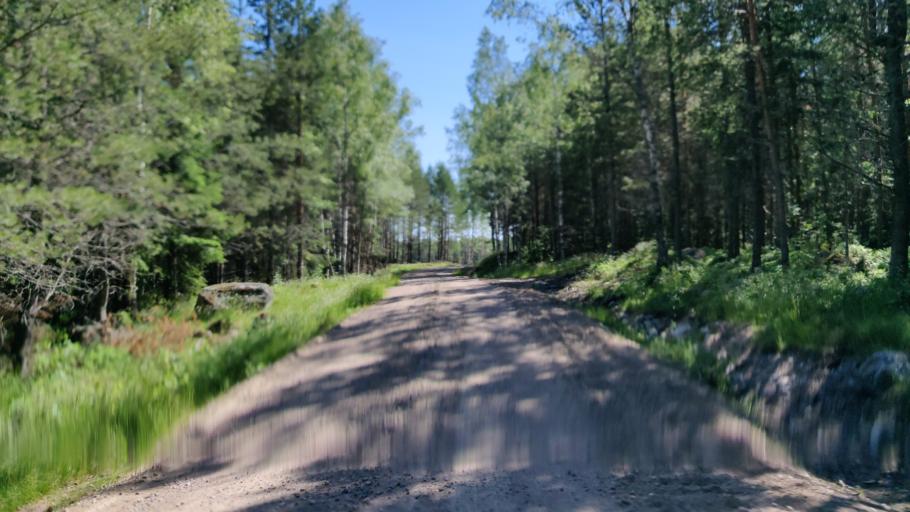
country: SE
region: Vaermland
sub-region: Hagfors Kommun
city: Hagfors
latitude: 59.9856
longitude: 13.5989
